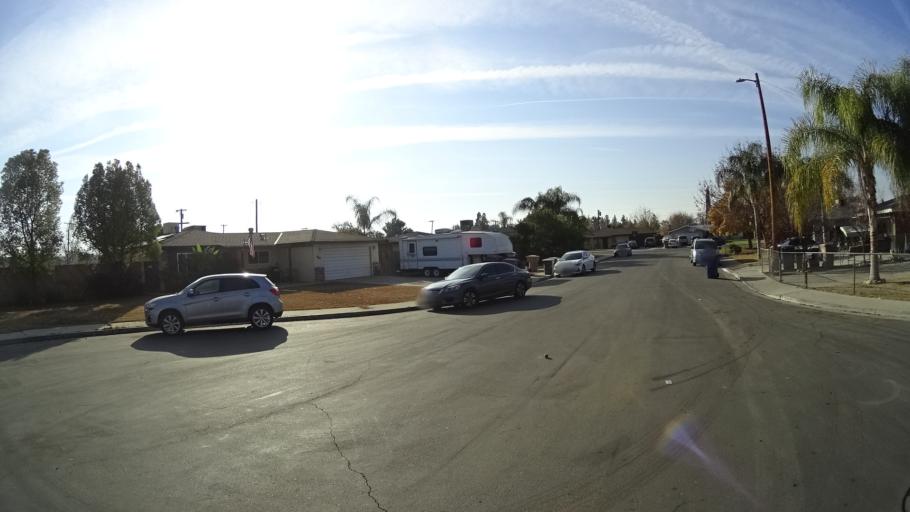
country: US
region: California
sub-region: Kern County
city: Bakersfield
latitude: 35.3209
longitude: -119.0226
